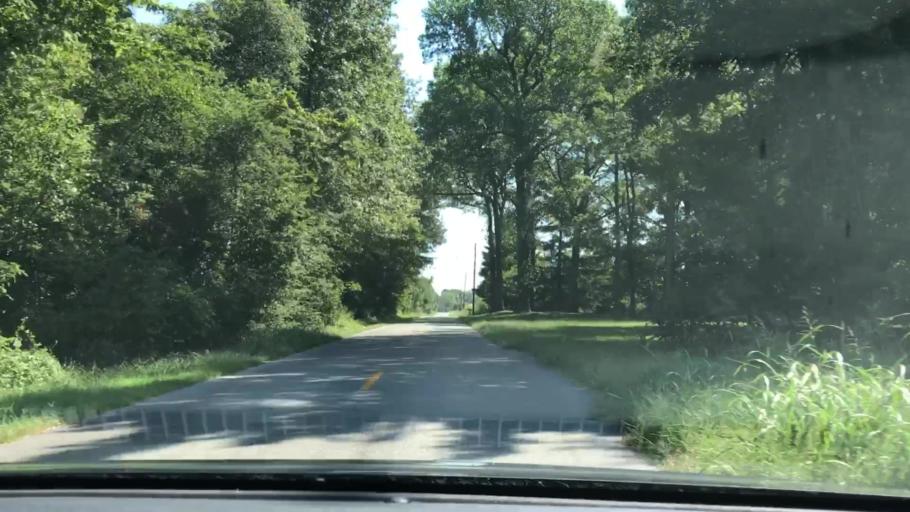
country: US
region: Kentucky
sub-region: Fulton County
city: Fulton
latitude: 36.5219
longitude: -88.8969
